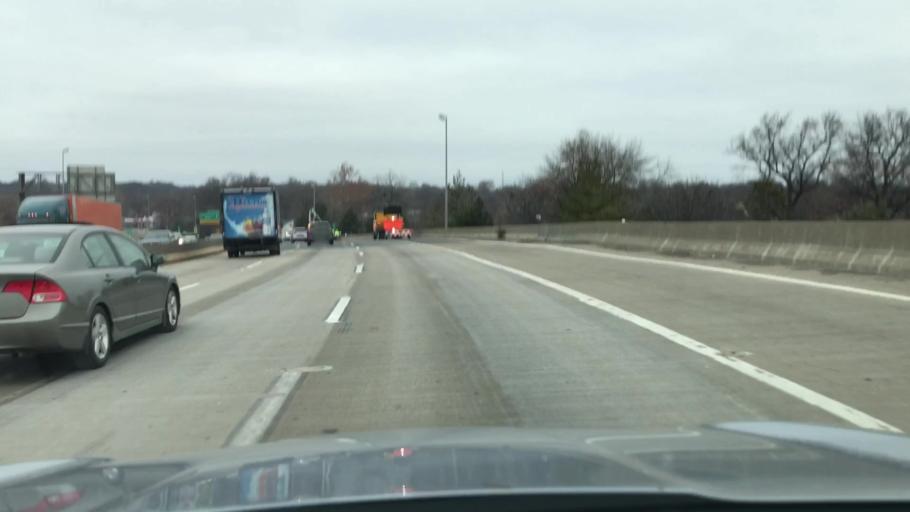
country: US
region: Missouri
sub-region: Saint Louis County
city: Pine Lawn
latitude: 38.6982
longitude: -90.2609
